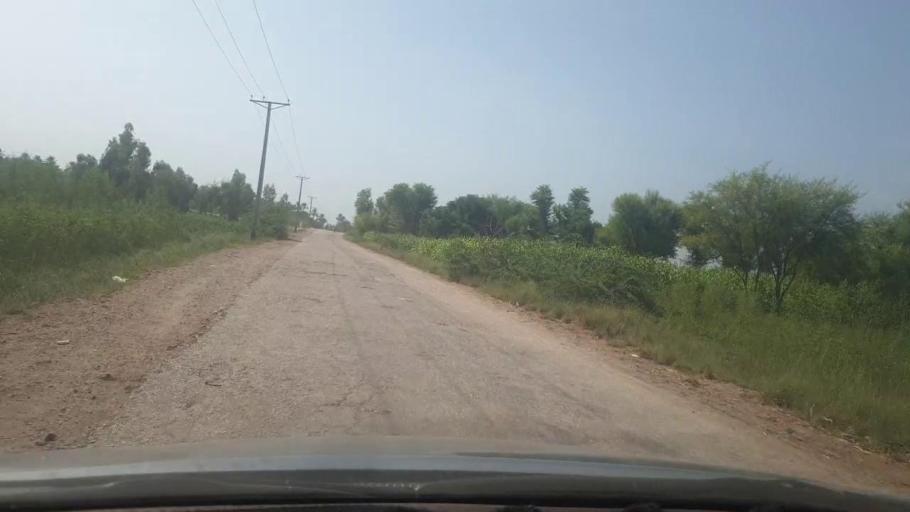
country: PK
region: Sindh
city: Gambat
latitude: 27.3293
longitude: 68.5501
